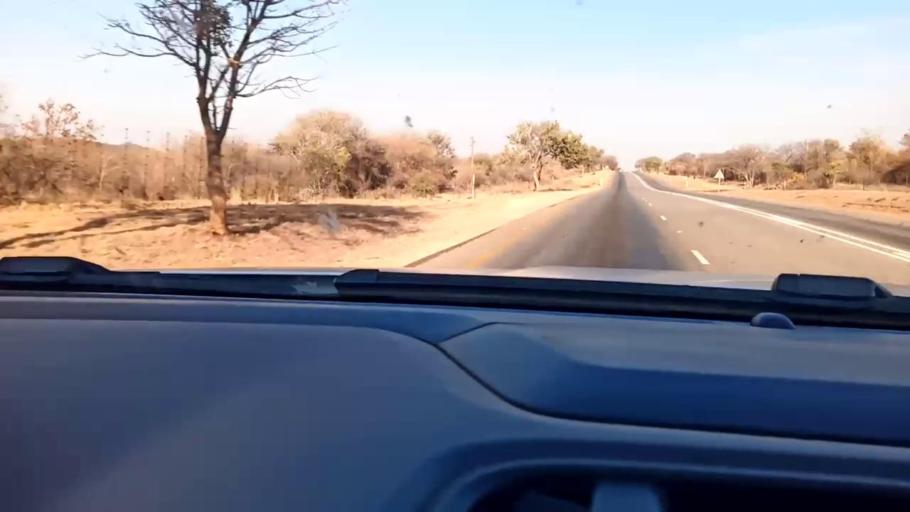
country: ZA
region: Limpopo
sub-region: Mopani District Municipality
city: Duiwelskloof
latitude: -23.6179
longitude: 30.1207
